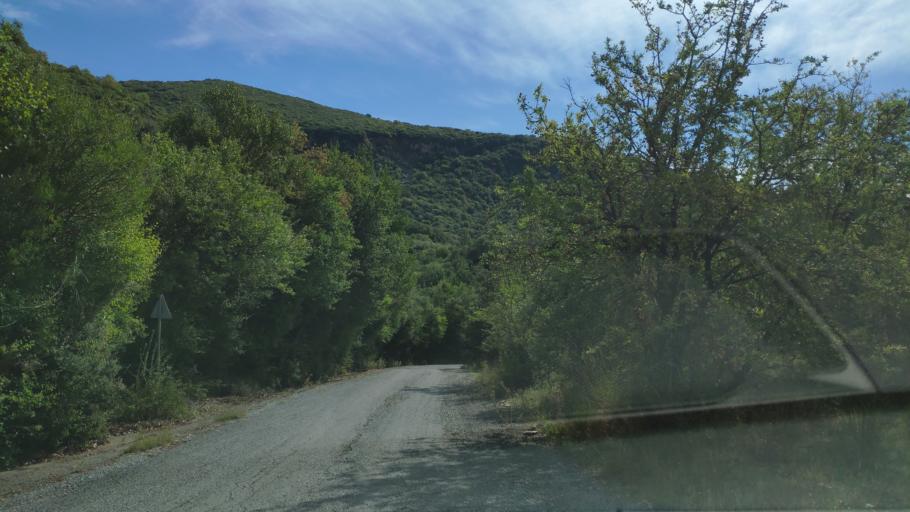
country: GR
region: Peloponnese
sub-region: Nomos Arkadias
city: Dimitsana
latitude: 37.5362
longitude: 22.0509
